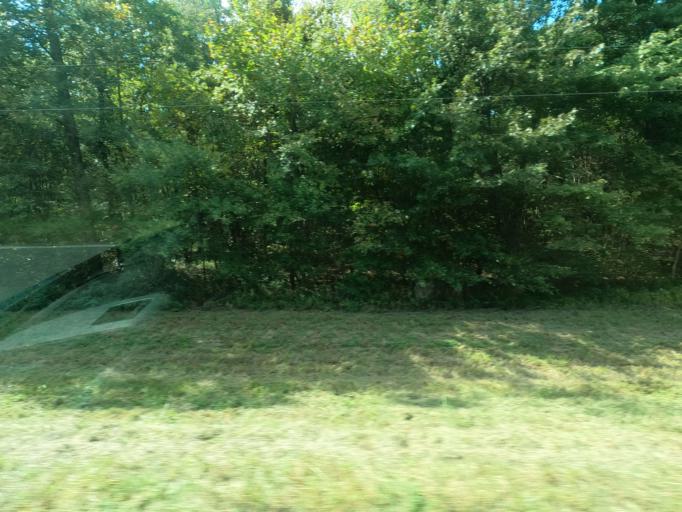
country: US
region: Illinois
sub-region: Massac County
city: Metropolis
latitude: 37.2859
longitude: -88.7574
